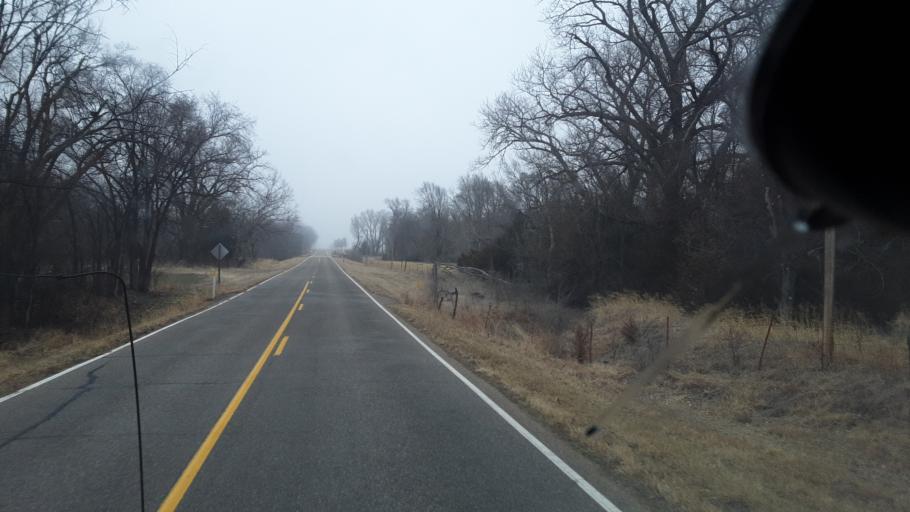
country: US
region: Kansas
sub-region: Reno County
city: South Hutchinson
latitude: 37.8992
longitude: -98.0137
